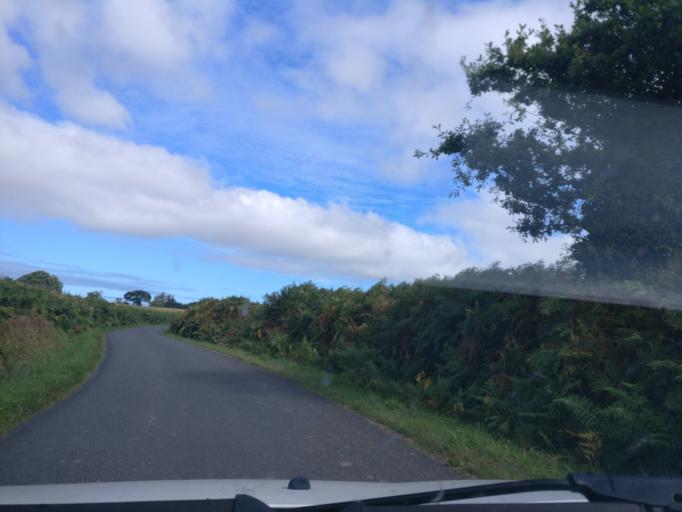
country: FR
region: Brittany
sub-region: Departement des Cotes-d'Armor
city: Rospez
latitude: 48.7486
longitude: -3.3740
